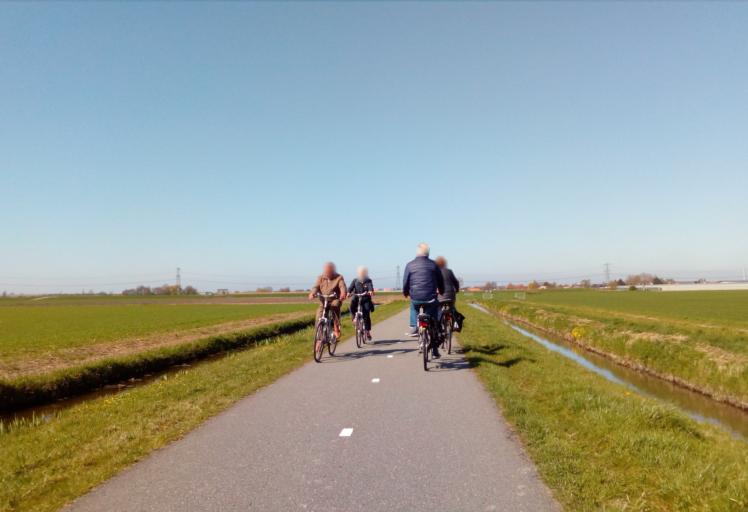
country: NL
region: South Holland
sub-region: Gemeente Westland
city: Kwintsheul
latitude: 51.9986
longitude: 4.2938
